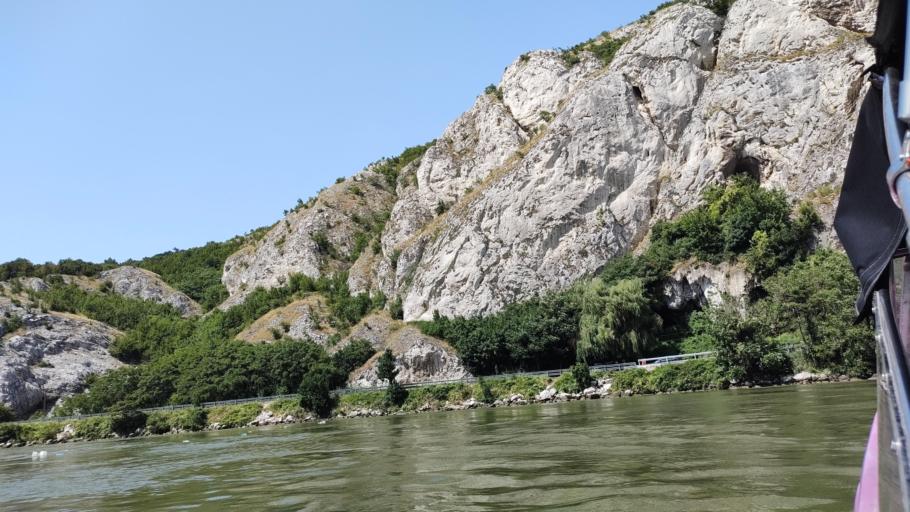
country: RO
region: Caras-Severin
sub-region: Comuna Pescari
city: Coronini
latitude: 44.6637
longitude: 21.6988
